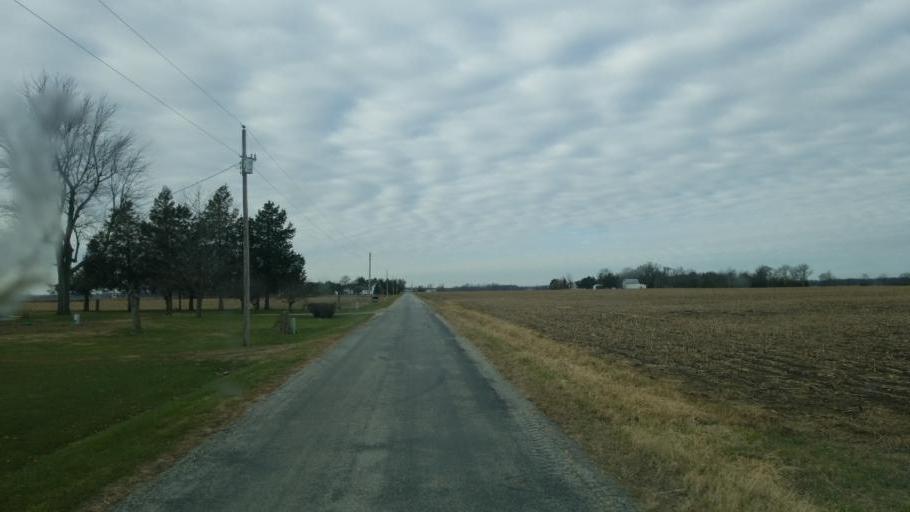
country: US
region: Ohio
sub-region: Union County
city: Richwood
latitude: 40.5498
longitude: -83.2992
